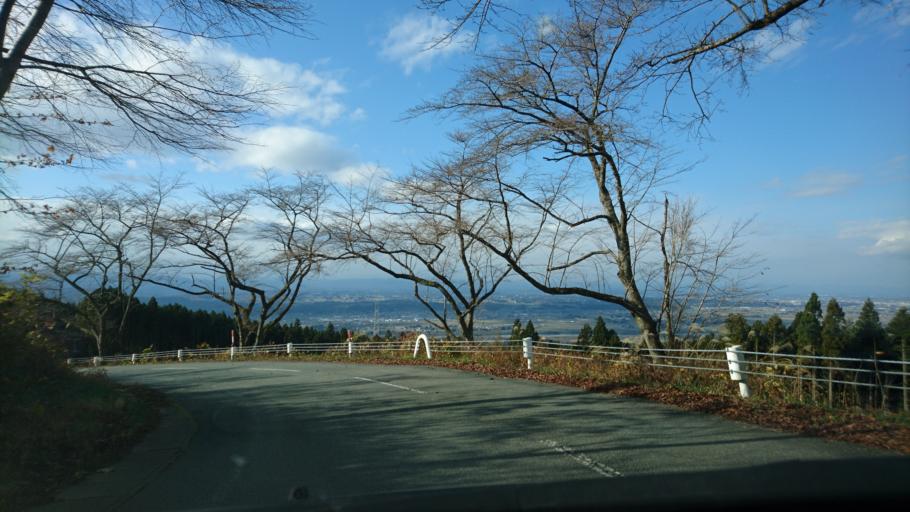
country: JP
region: Iwate
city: Ichinoseki
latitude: 39.0249
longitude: 141.1791
